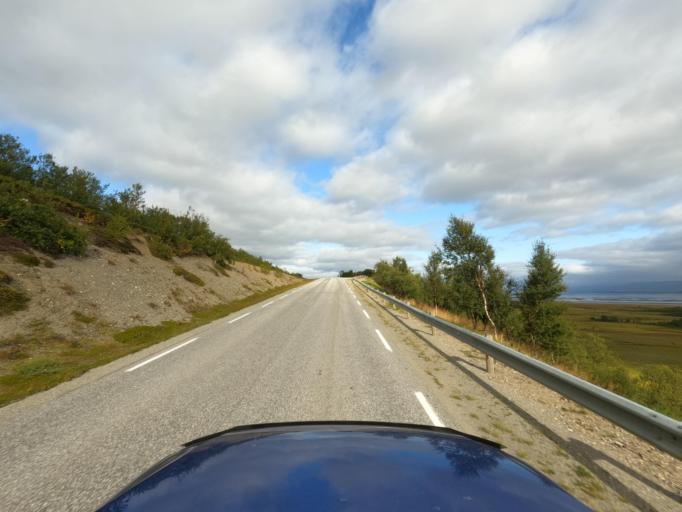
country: NO
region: Finnmark Fylke
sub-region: Porsanger
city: Lakselv
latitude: 70.1586
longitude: 24.8940
